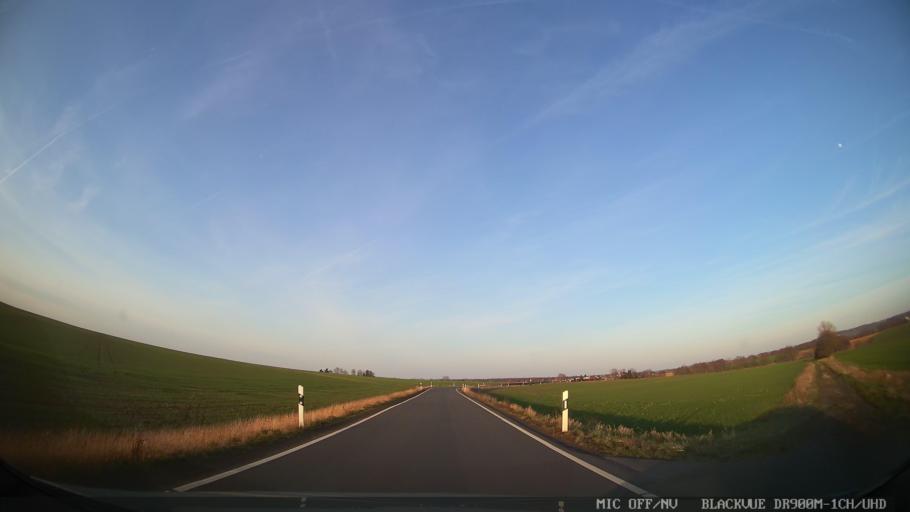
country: DE
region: Hesse
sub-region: Regierungsbezirk Darmstadt
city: Gross-Zimmern
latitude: 49.8610
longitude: 8.8790
